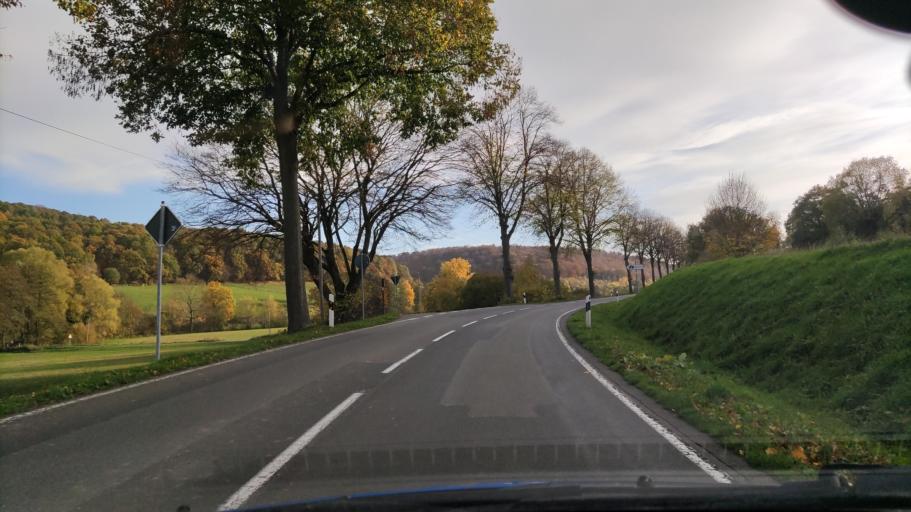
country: DE
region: Lower Saxony
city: Dassel
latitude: 51.7585
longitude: 9.7612
